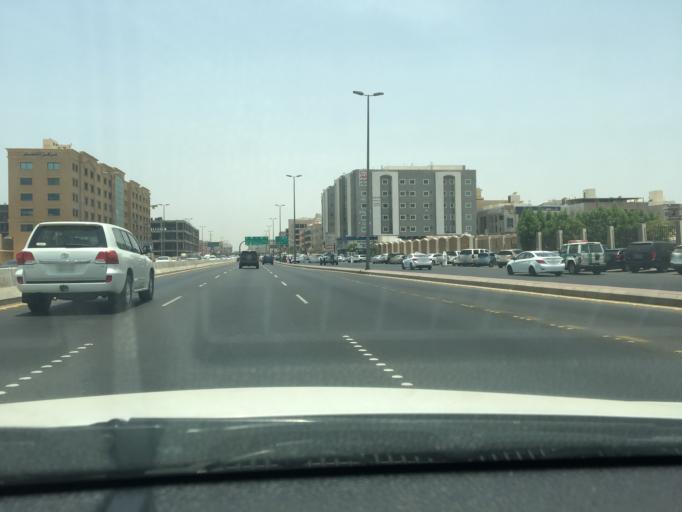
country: SA
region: Makkah
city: Jeddah
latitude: 21.5525
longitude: 39.1887
